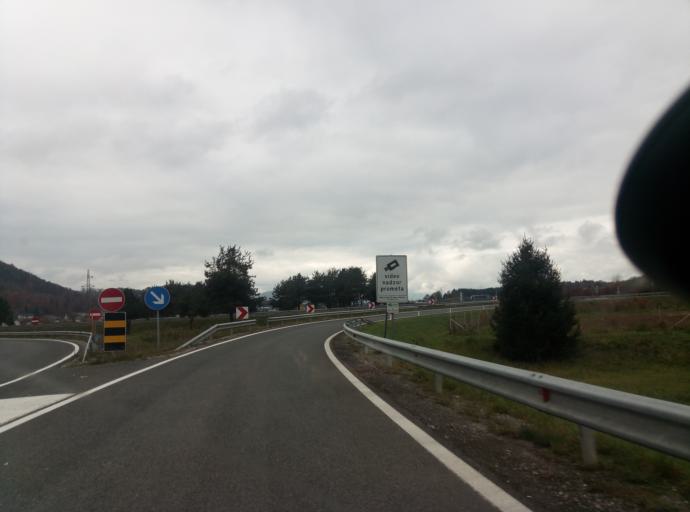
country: SI
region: Vodice
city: Vodice
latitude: 46.1836
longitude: 14.4854
